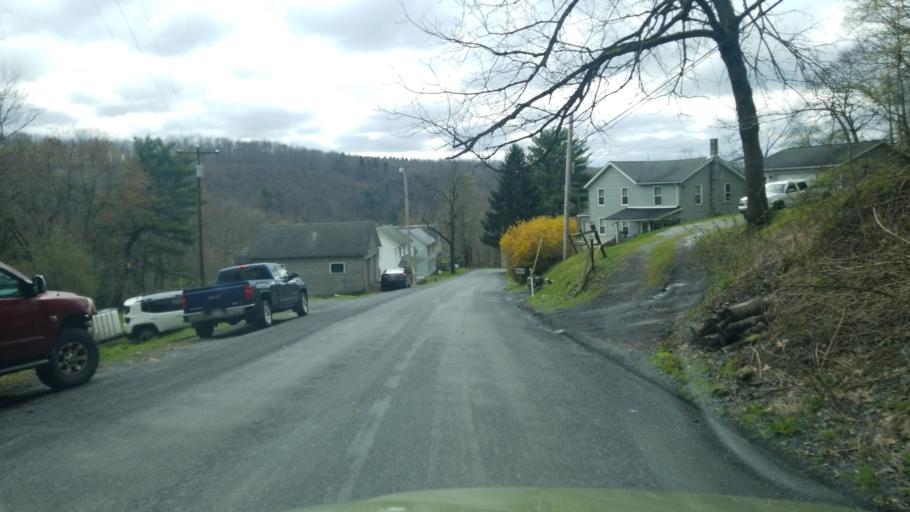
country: US
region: Pennsylvania
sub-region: Clearfield County
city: Shiloh
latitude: 41.0730
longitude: -78.3633
